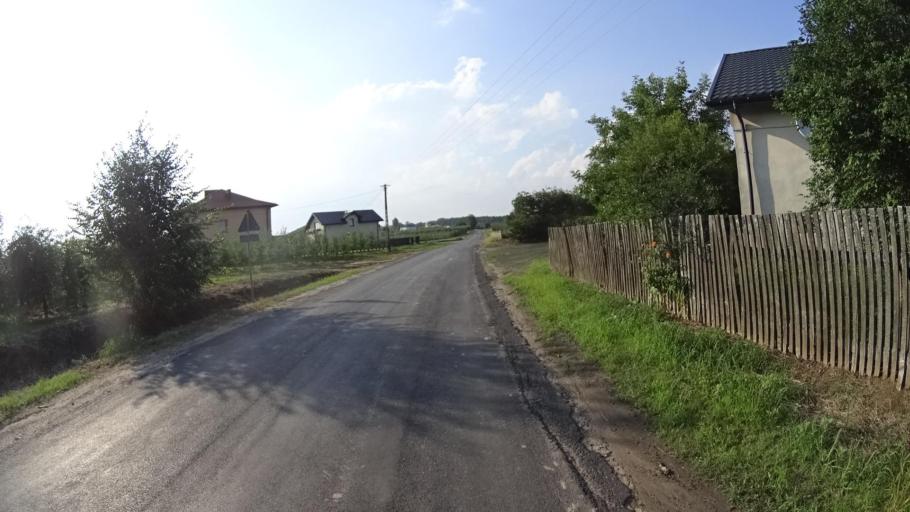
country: PL
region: Masovian Voivodeship
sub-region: Powiat grojecki
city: Goszczyn
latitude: 51.7088
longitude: 20.7926
